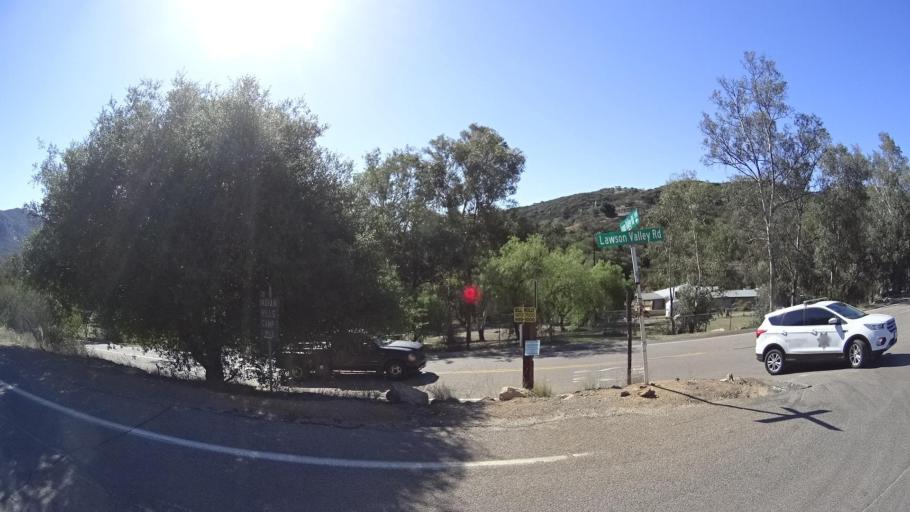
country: US
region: California
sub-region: San Diego County
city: Jamul
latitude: 32.7306
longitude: -116.8216
